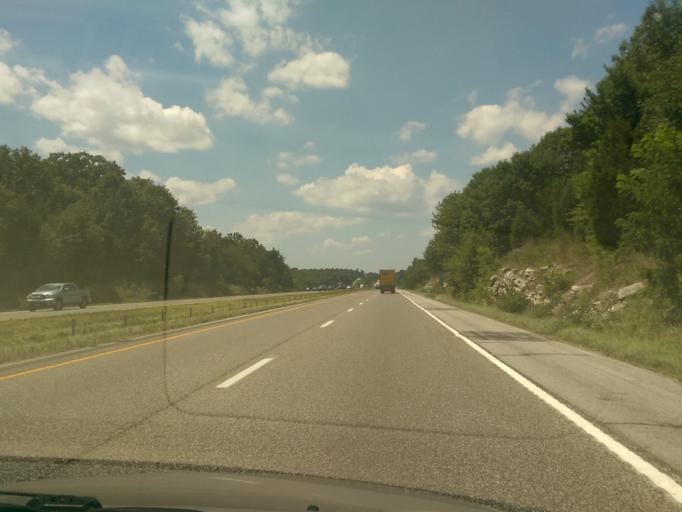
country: US
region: Missouri
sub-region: Boone County
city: Columbia
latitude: 38.9728
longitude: -92.4653
